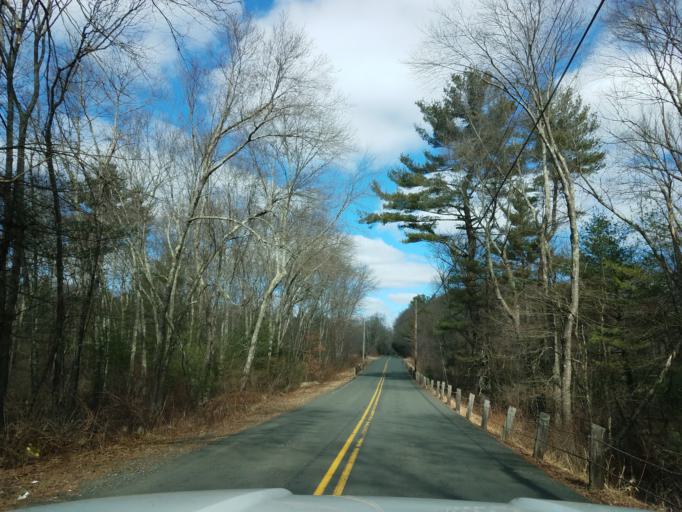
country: US
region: Massachusetts
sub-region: Worcester County
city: Dudley
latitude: 42.0158
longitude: -71.9147
